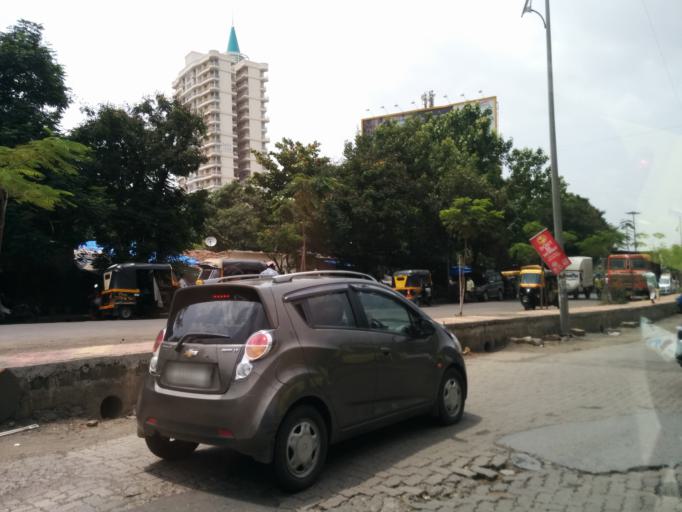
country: IN
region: Maharashtra
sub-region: Thane
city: Thane
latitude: 19.2126
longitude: 72.9769
